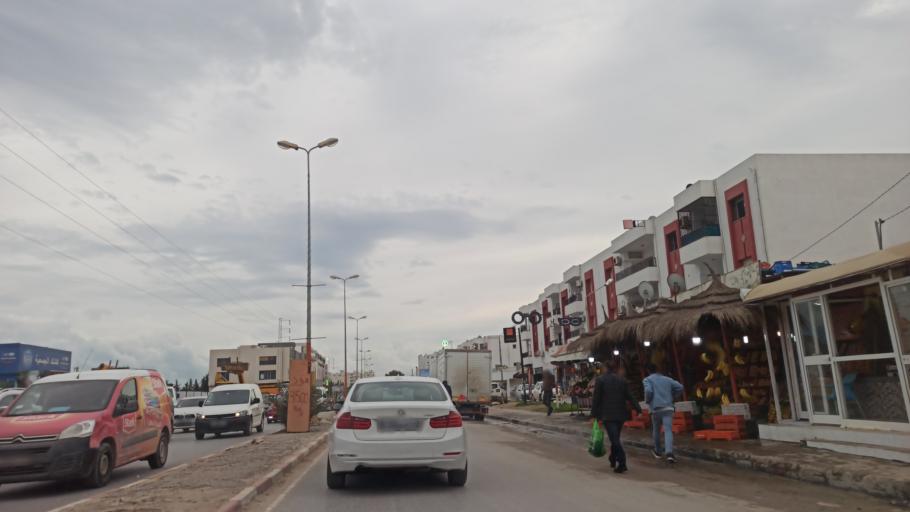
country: TN
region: Ariana
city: Ariana
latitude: 36.8660
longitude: 10.2518
